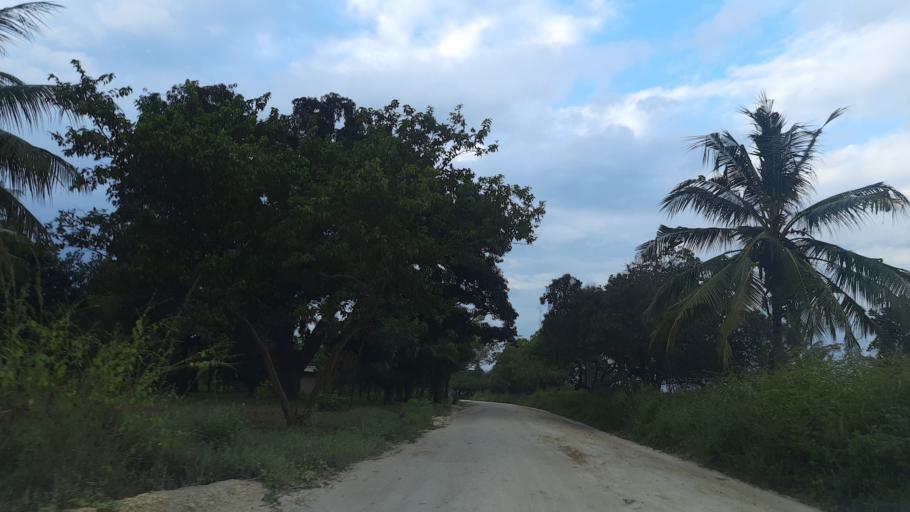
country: TZ
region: Pwani
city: Bagamoyo
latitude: -6.5192
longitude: 38.9272
